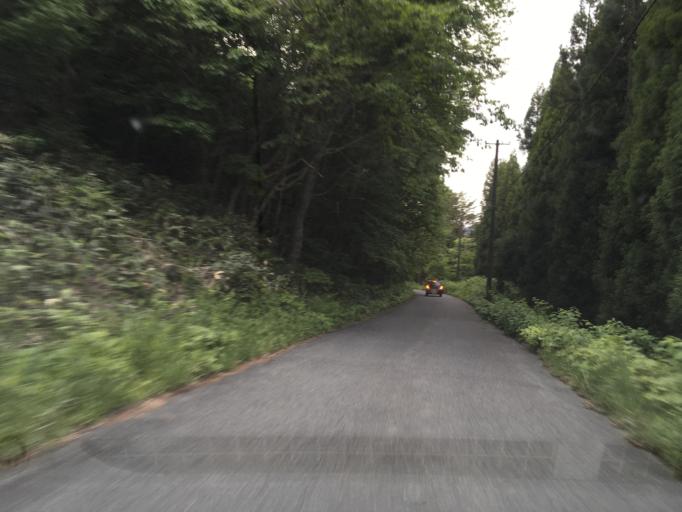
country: JP
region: Iwate
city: Mizusawa
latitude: 39.1444
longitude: 141.3069
